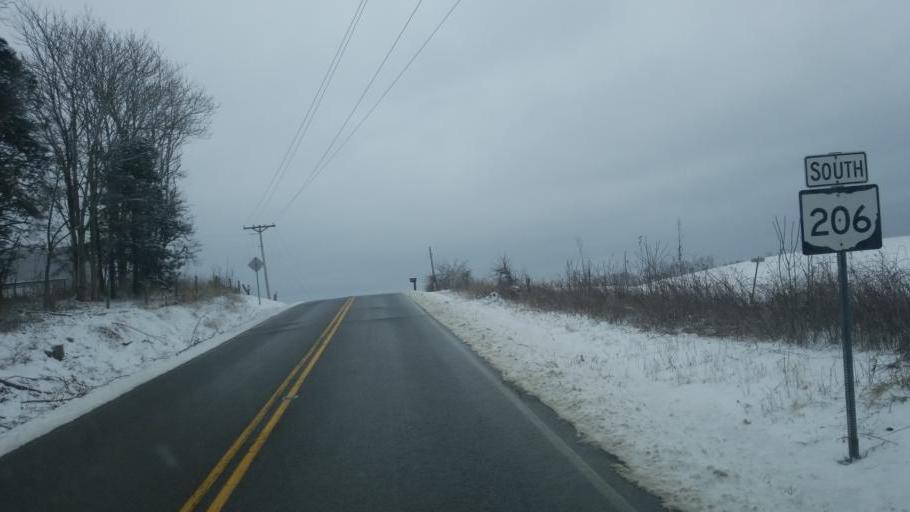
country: US
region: Ohio
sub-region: Knox County
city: Oak Hill
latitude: 40.4374
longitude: -82.1428
